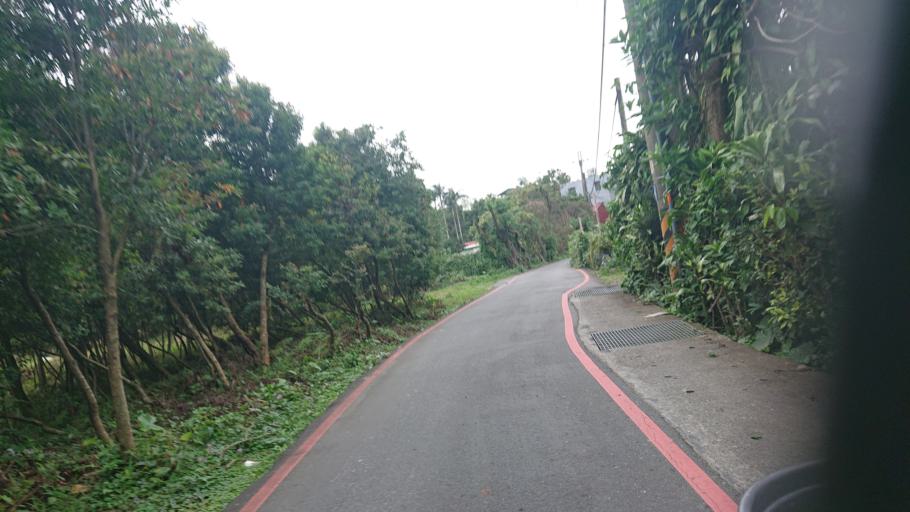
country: TW
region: Taiwan
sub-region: Taoyuan
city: Taoyuan
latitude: 24.9500
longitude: 121.3718
